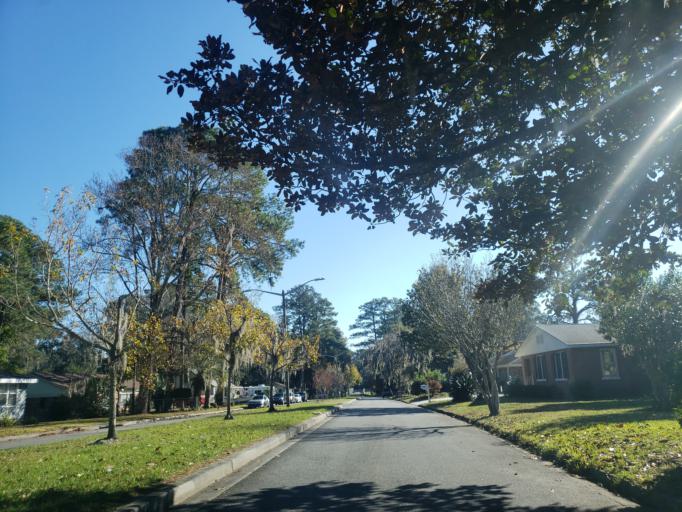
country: US
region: Georgia
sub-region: Chatham County
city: Isle of Hope
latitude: 31.9960
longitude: -81.1041
